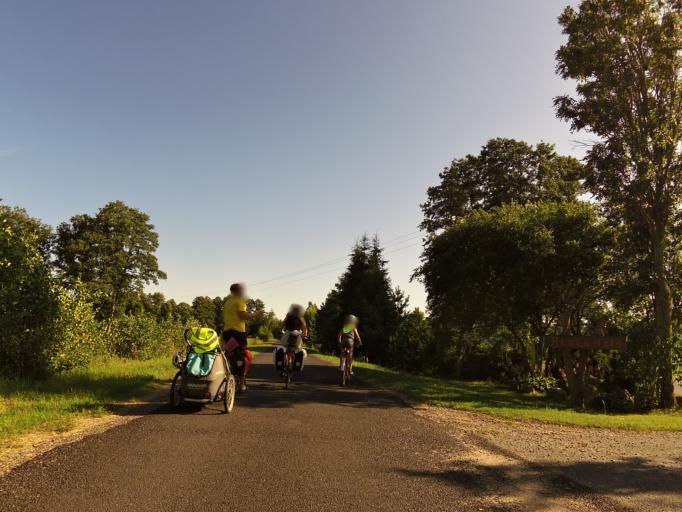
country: EE
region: Hiiumaa
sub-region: Kaerdla linn
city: Kardla
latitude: 58.7792
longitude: 22.4858
